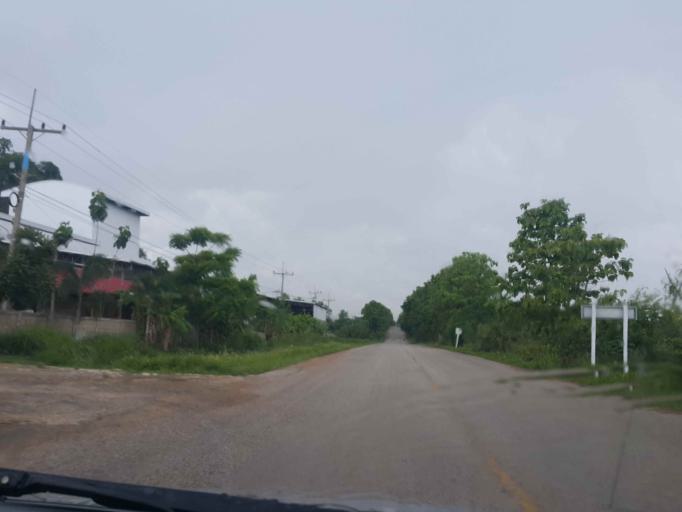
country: TH
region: Phayao
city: Dok Kham Tai
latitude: 19.0142
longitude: 100.0622
